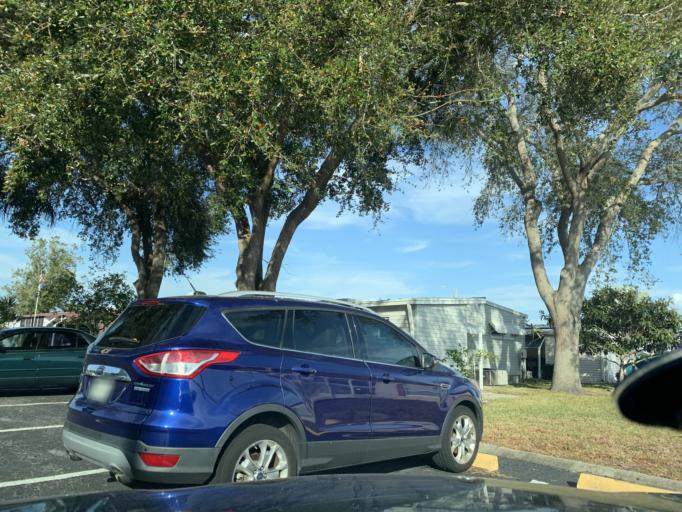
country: US
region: Florida
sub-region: Pinellas County
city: Largo
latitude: 27.9005
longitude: -82.7930
